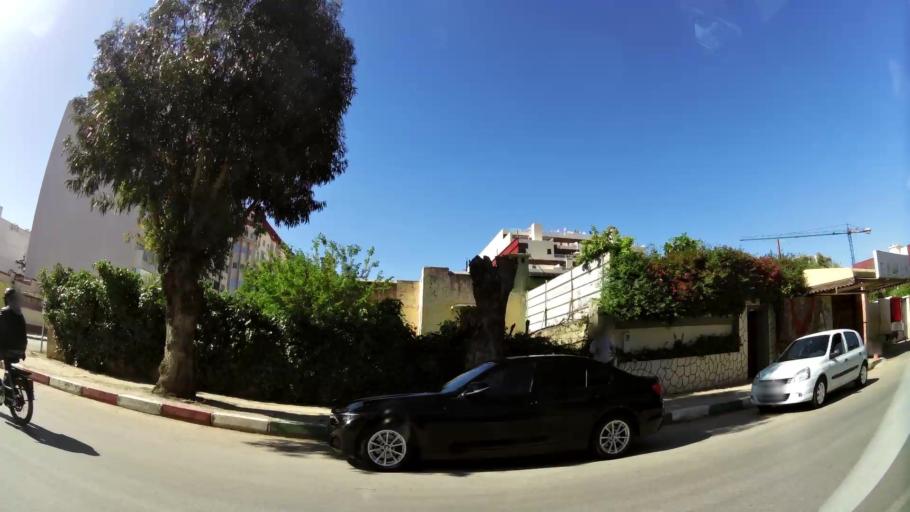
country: MA
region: Meknes-Tafilalet
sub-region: Meknes
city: Meknes
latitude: 33.8922
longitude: -5.5359
